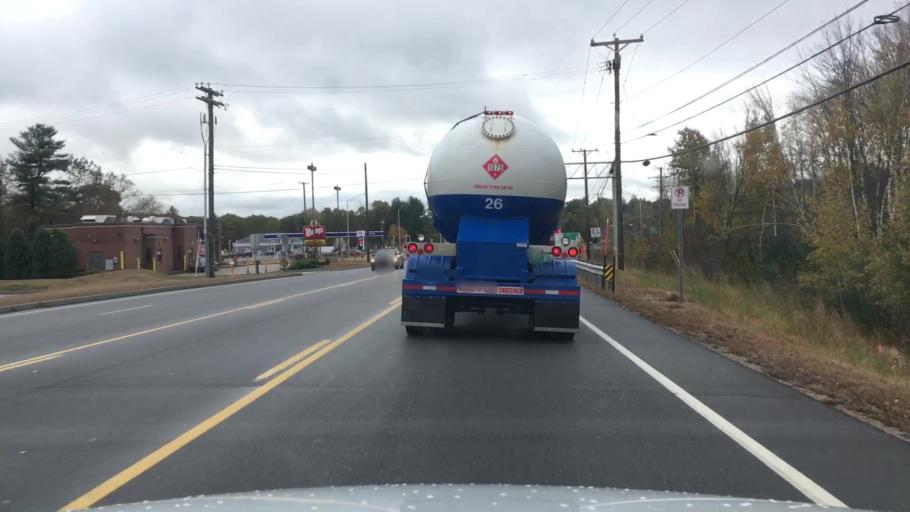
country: US
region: New Hampshire
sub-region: Strafford County
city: Lee
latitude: 43.1508
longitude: -71.0062
